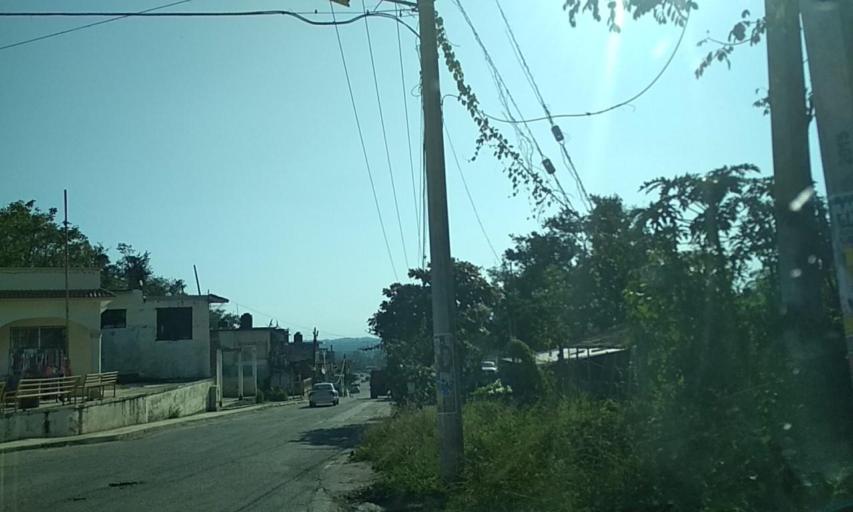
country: MX
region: Veracruz
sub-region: Papantla
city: El Chote
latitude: 20.4056
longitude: -97.3378
